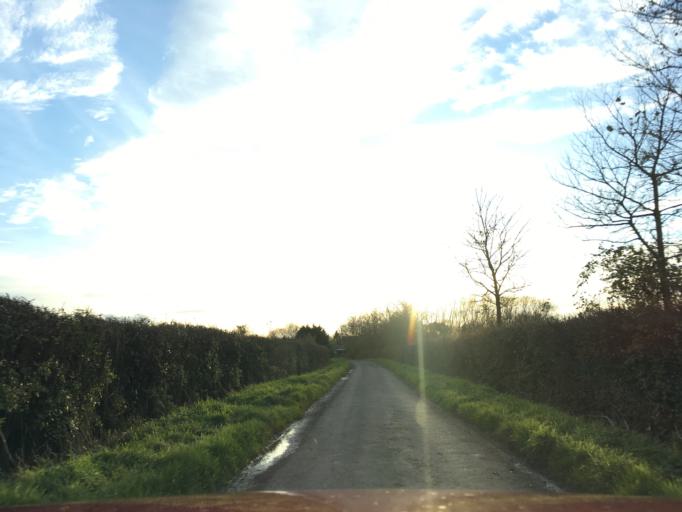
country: GB
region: England
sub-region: South Gloucestershire
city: Hill
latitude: 51.6639
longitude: -2.5506
